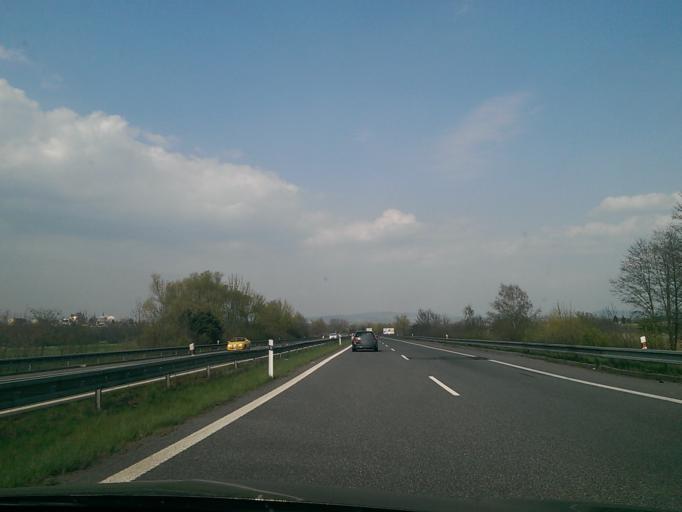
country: CZ
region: Central Bohemia
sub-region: Okres Mlada Boleslav
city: Zd'ar
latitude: 50.5597
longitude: 15.0509
